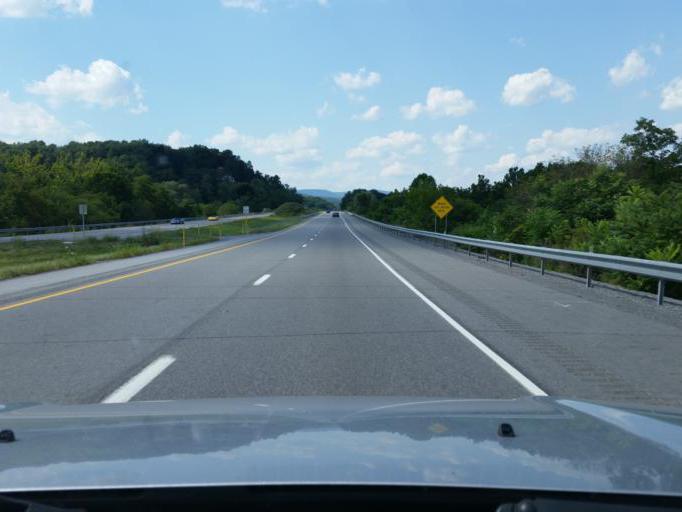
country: US
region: Pennsylvania
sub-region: Blair County
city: Duncansville
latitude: 40.4276
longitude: -78.4244
